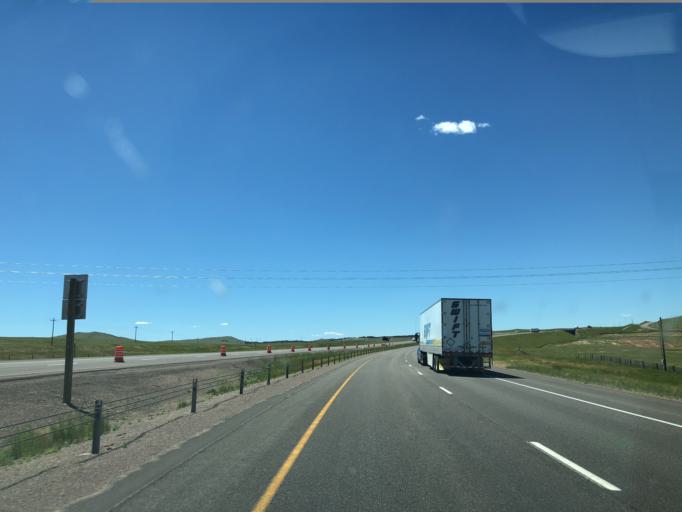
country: US
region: Wyoming
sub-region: Laramie County
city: Cheyenne
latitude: 41.0953
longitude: -105.1986
